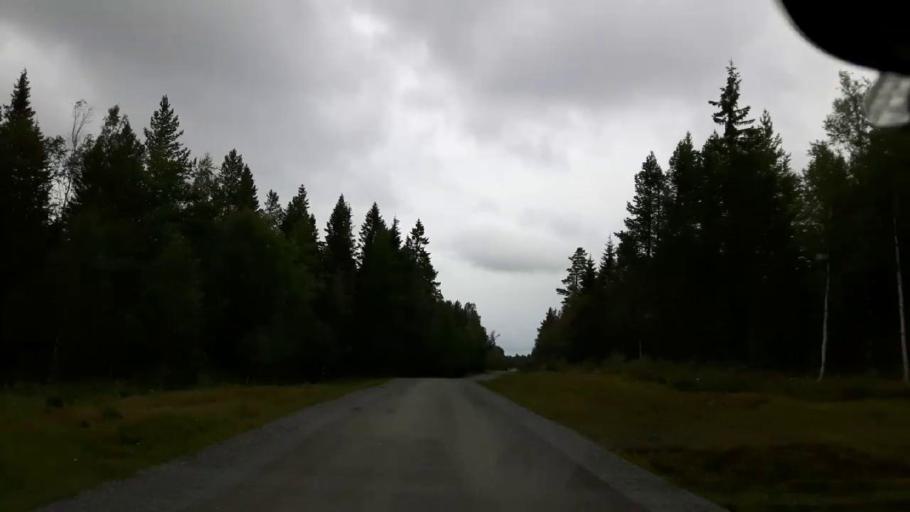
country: SE
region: Jaemtland
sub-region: OEstersunds Kommun
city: Ostersund
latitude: 63.0706
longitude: 14.5530
